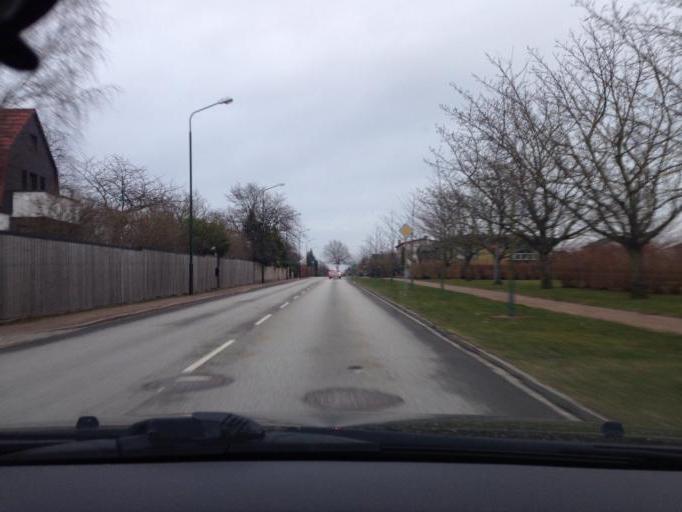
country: SE
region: Skane
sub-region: Malmo
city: Malmoe
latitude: 55.5829
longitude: 12.9646
